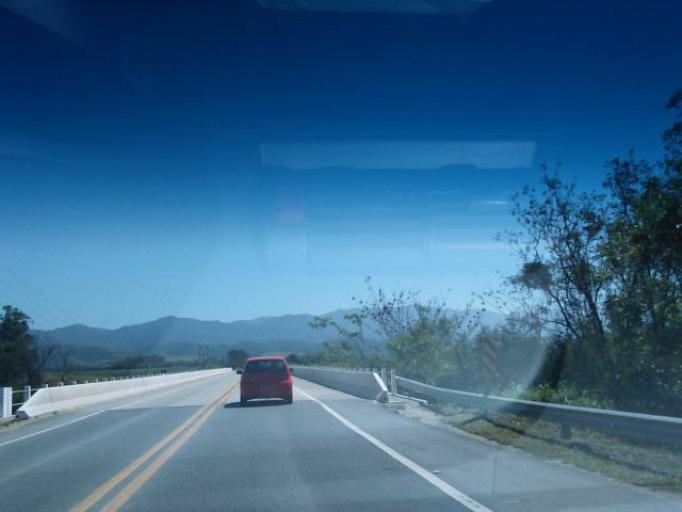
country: BR
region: Sao Paulo
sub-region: Taubate
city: Taubate
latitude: -22.9990
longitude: -45.6409
